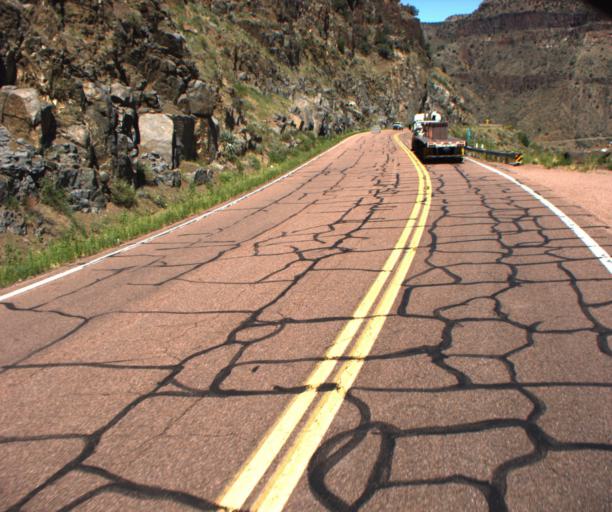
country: US
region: Arizona
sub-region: Navajo County
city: Cibecue
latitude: 33.7906
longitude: -110.4949
